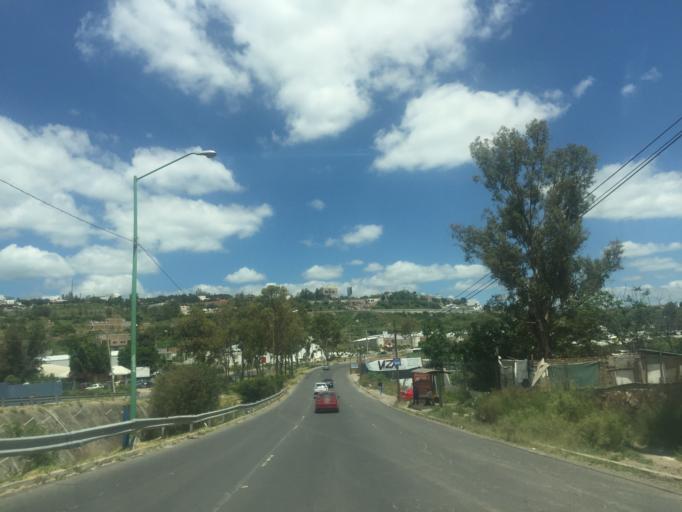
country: MX
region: Guanajuato
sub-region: Leon
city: La Ermita
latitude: 21.1418
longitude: -101.7190
